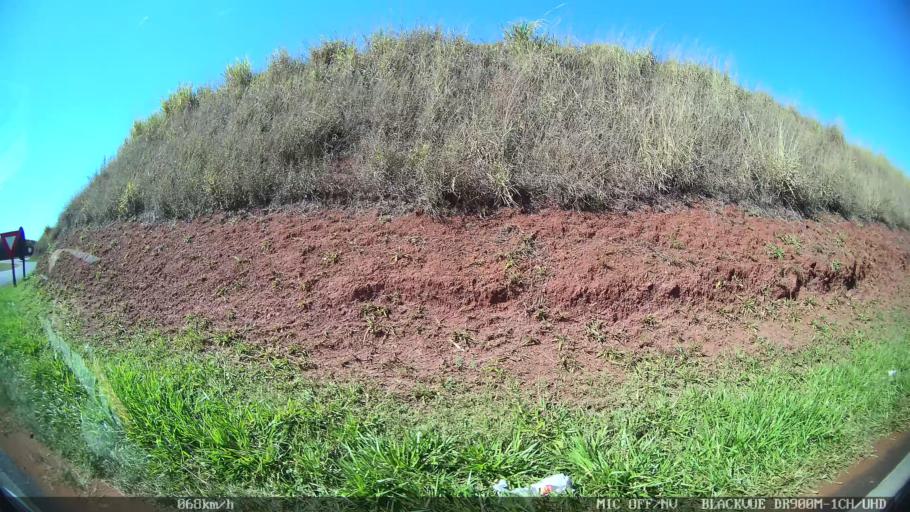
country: BR
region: Sao Paulo
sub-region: Franca
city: Franca
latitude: -20.6775
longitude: -47.4953
